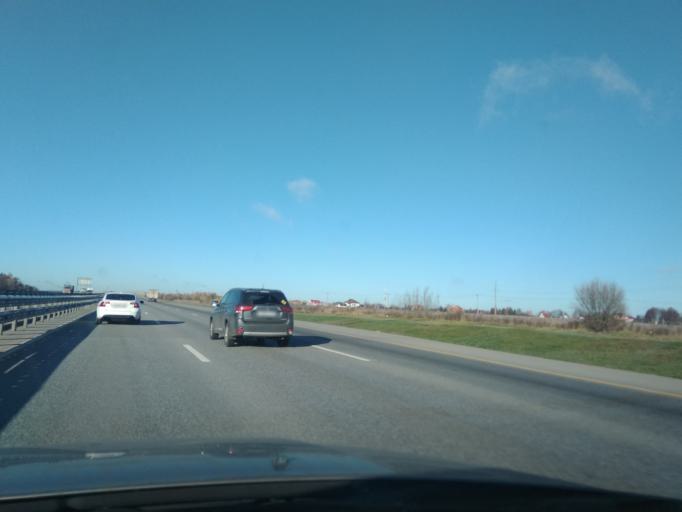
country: RU
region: Moskovskaya
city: Yershovo
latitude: 55.8273
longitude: 36.8947
